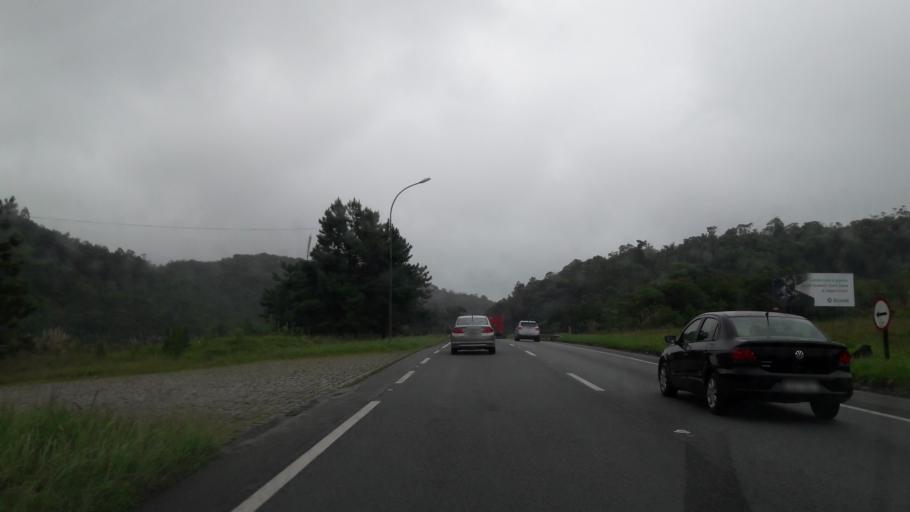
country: BR
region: Parana
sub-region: Campina Grande Do Sul
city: Campina Grande do Sul
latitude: -25.1064
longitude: -48.8058
